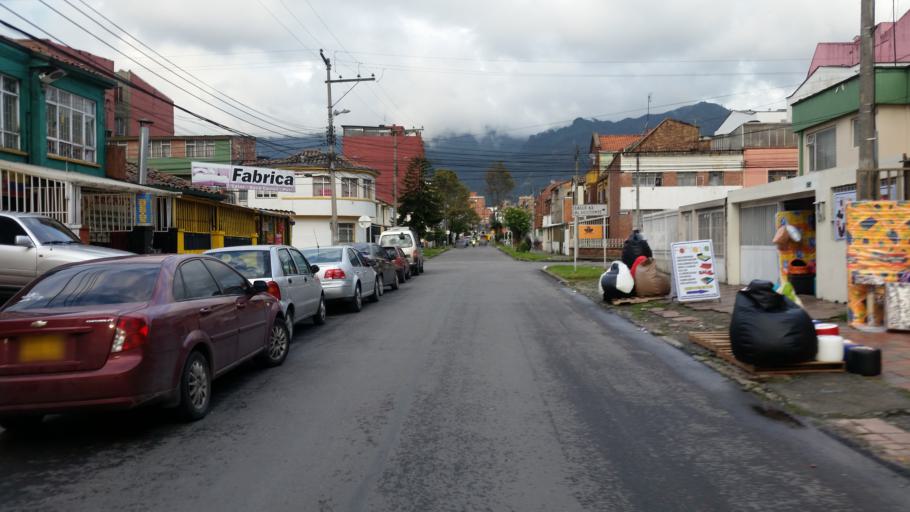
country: CO
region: Bogota D.C.
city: Bogota
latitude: 4.6520
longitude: -74.0720
